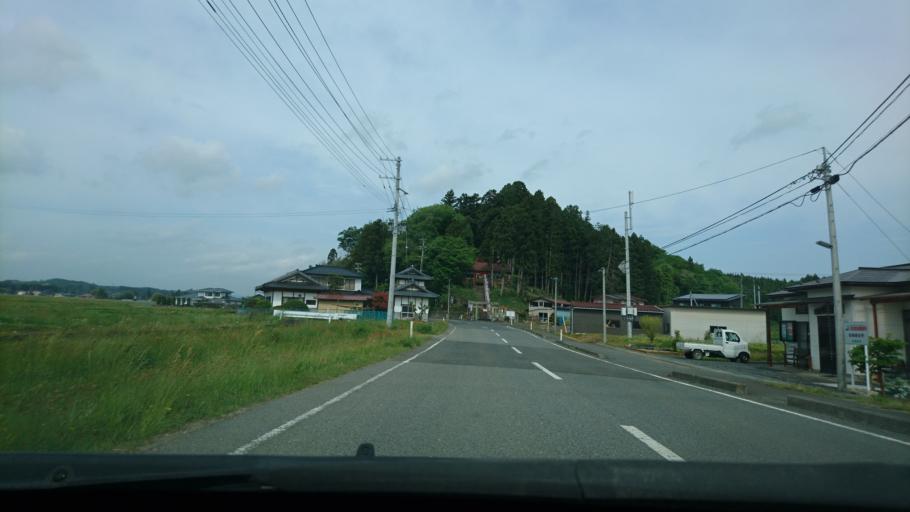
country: JP
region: Iwate
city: Ichinoseki
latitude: 38.8217
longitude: 141.0444
